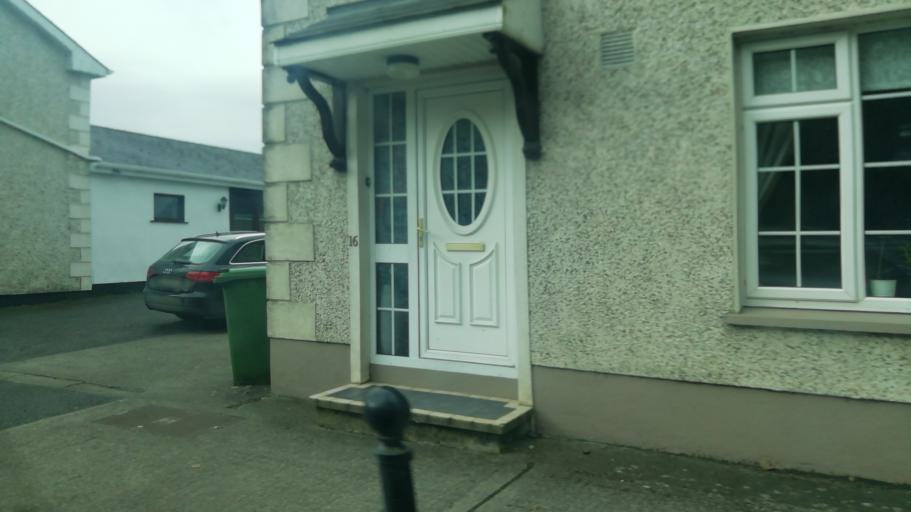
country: IE
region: Leinster
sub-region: Kildare
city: Rathangan
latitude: 53.2219
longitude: -6.9915
